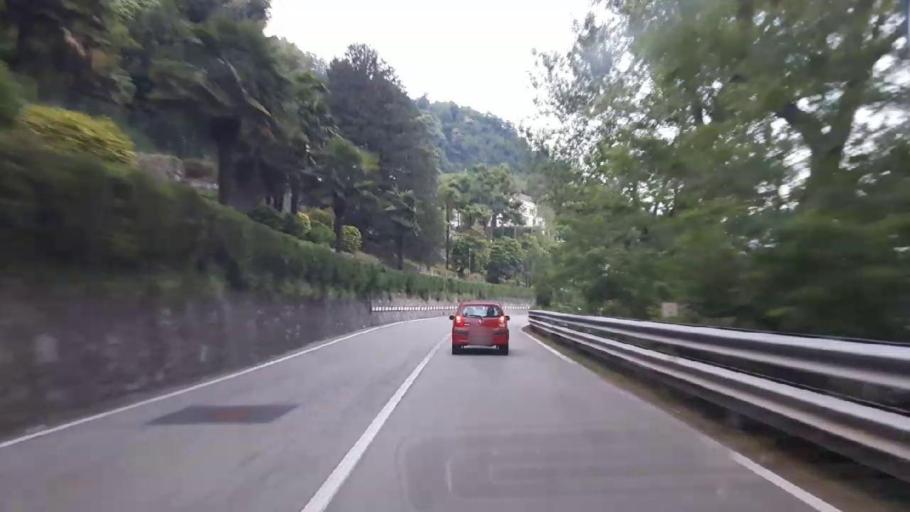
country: IT
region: Piedmont
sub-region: Provincia di Novara
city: Massino Visconti
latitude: 45.8137
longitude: 8.5449
